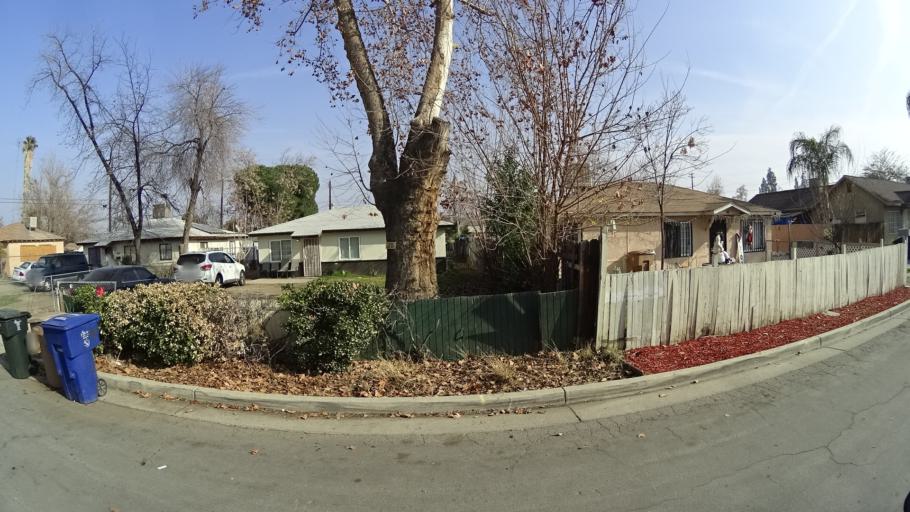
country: US
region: California
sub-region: Kern County
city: Bakersfield
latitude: 35.3634
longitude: -119.0131
